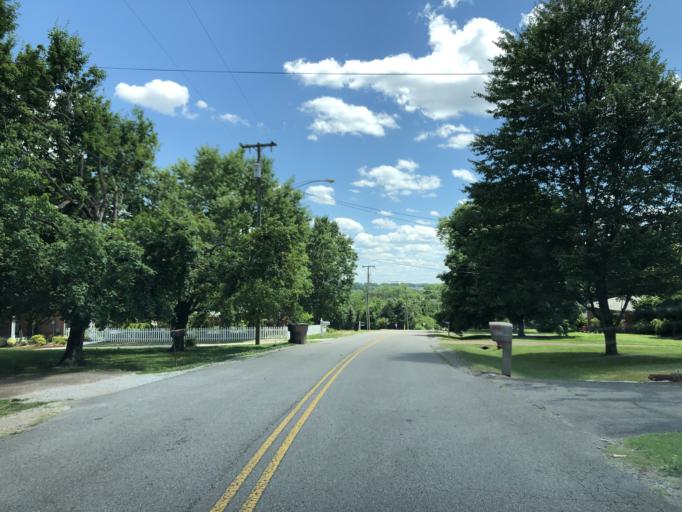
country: US
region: Tennessee
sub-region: Davidson County
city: Nashville
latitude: 36.1773
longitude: -86.7191
